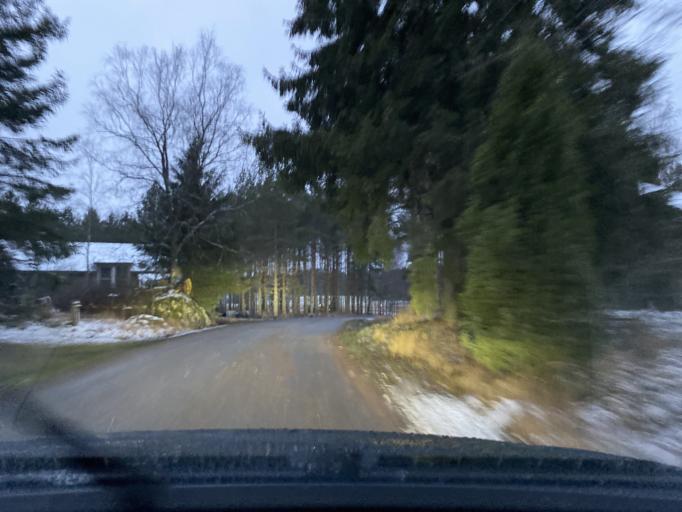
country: FI
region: Pirkanmaa
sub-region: Lounais-Pirkanmaa
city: Punkalaidun
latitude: 61.1629
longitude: 22.9633
